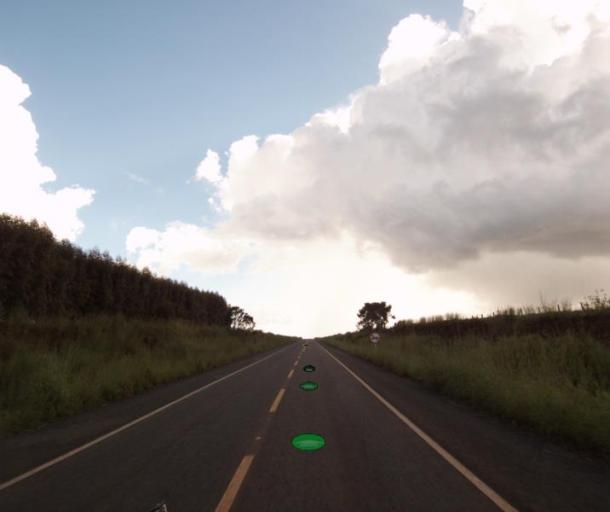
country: BR
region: Goias
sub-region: Itaberai
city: Itaberai
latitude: -15.9886
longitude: -49.7169
